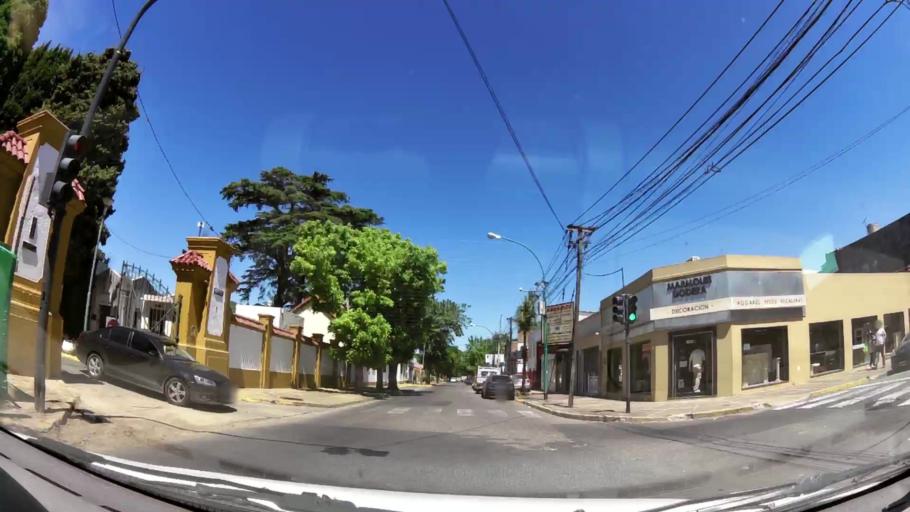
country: AR
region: Buenos Aires
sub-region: Partido de Vicente Lopez
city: Olivos
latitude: -34.5151
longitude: -58.5072
